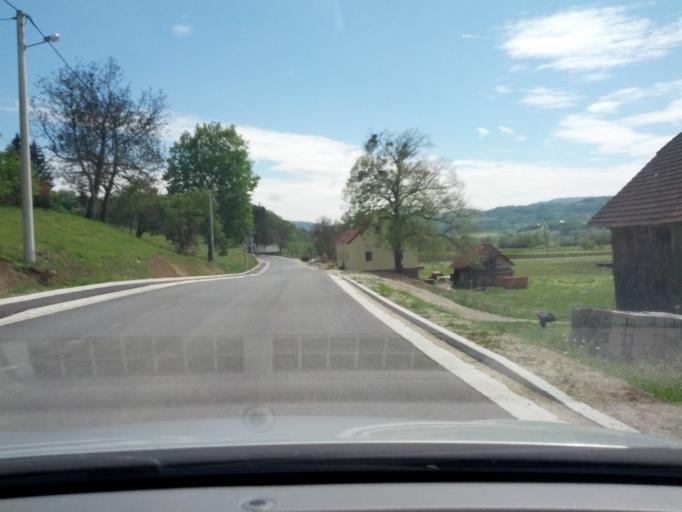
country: SI
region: Podcetrtek
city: Podcetrtek
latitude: 46.1101
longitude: 15.6214
